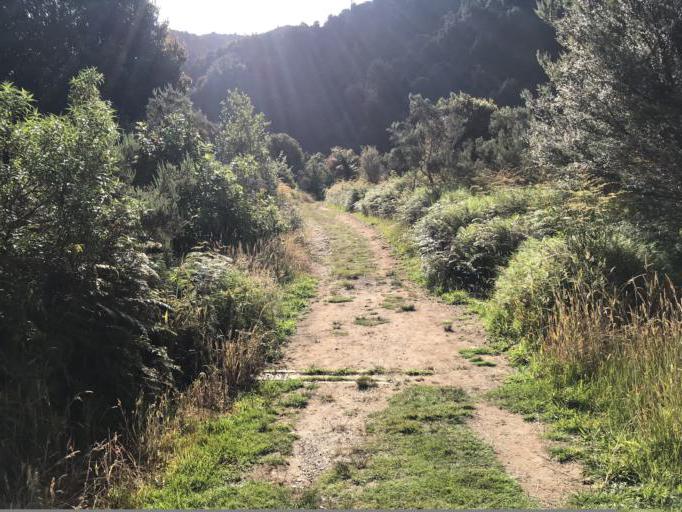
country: NZ
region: Wellington
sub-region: Kapiti Coast District
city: Otaki
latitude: -40.8713
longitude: 175.2329
